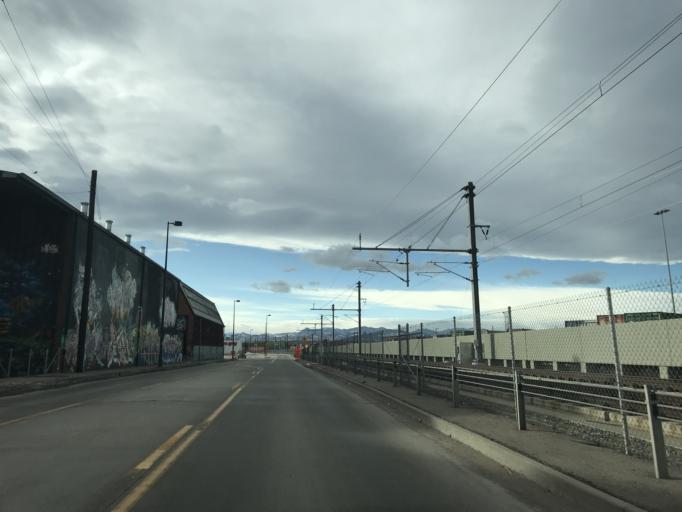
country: US
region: Colorado
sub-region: Denver County
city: Denver
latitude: 39.7729
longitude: -104.9673
